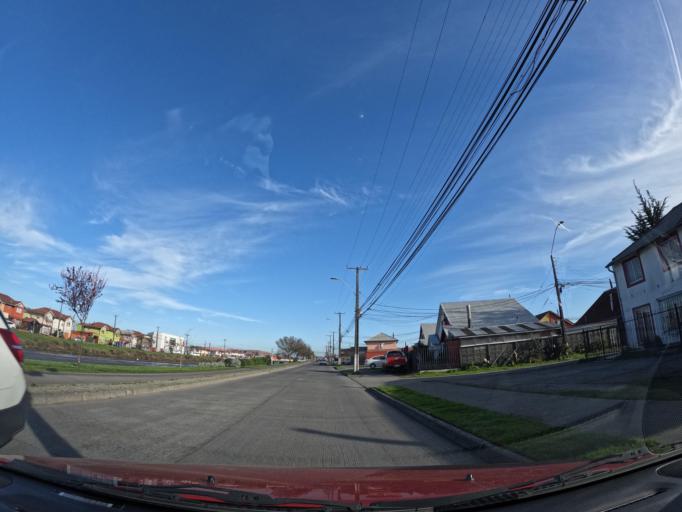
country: CL
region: Biobio
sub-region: Provincia de Concepcion
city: Talcahuano
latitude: -36.7487
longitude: -73.0845
